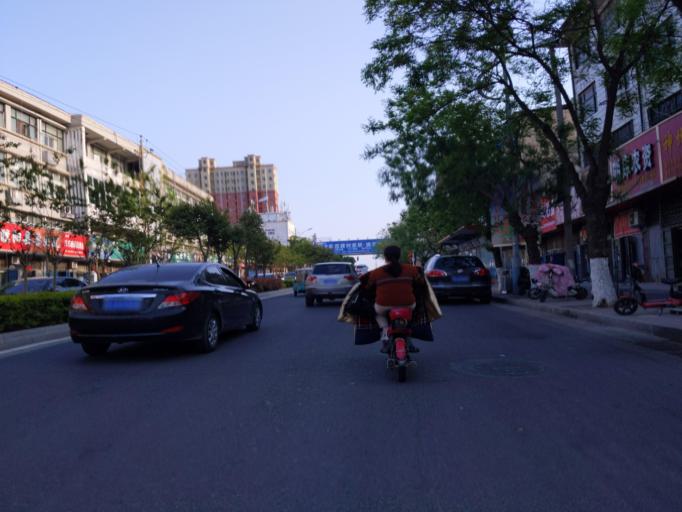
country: CN
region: Henan Sheng
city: Puyang Chengguanzhen
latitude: 35.6999
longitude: 115.0161
